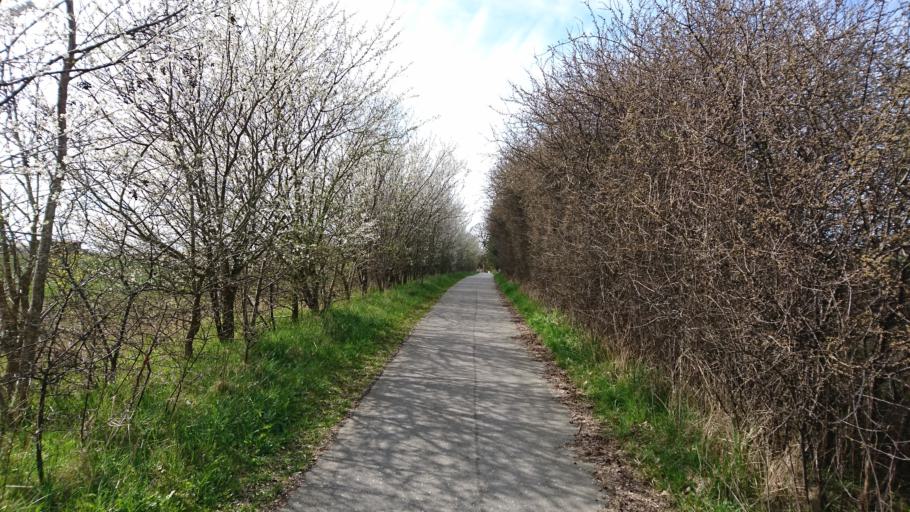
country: DK
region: Capital Region
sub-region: Egedal Kommune
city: Ganlose
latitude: 55.7953
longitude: 12.2434
